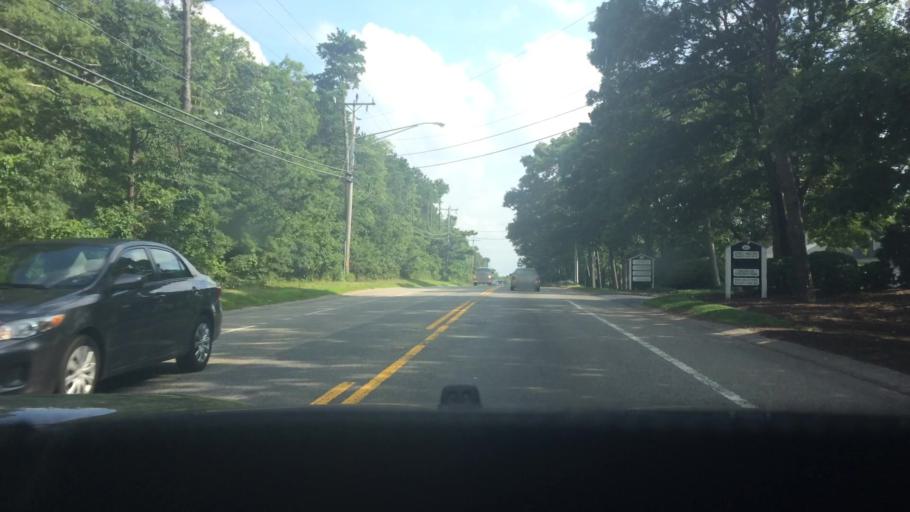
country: US
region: Massachusetts
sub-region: Barnstable County
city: Sandwich
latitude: 41.7344
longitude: -70.4915
